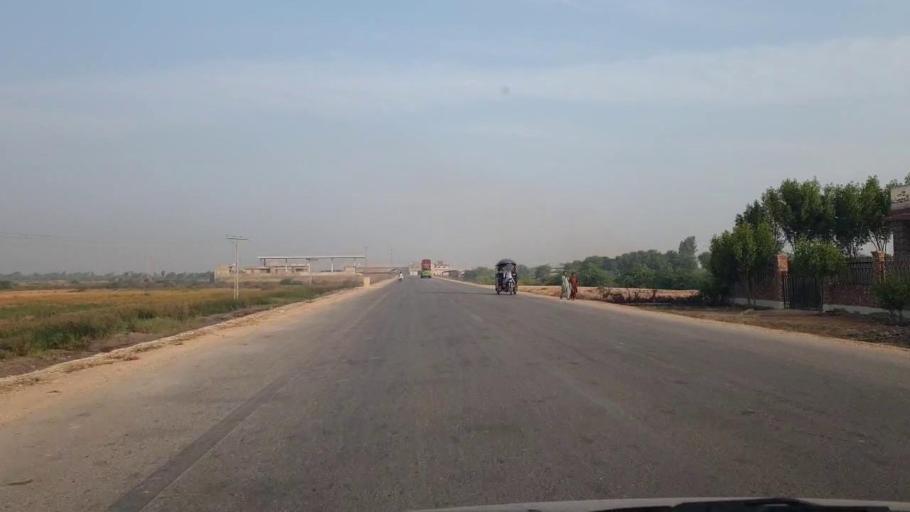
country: PK
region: Sindh
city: Badin
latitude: 24.6823
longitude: 68.8251
